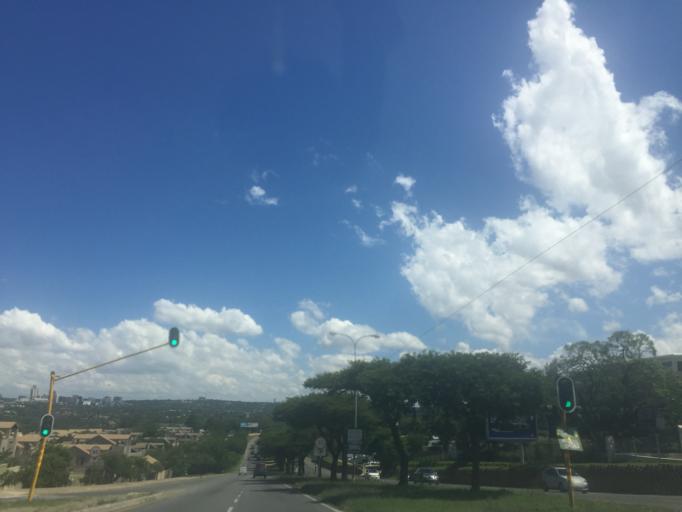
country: ZA
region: Gauteng
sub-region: City of Johannesburg Metropolitan Municipality
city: Midrand
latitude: -26.0671
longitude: 28.0254
